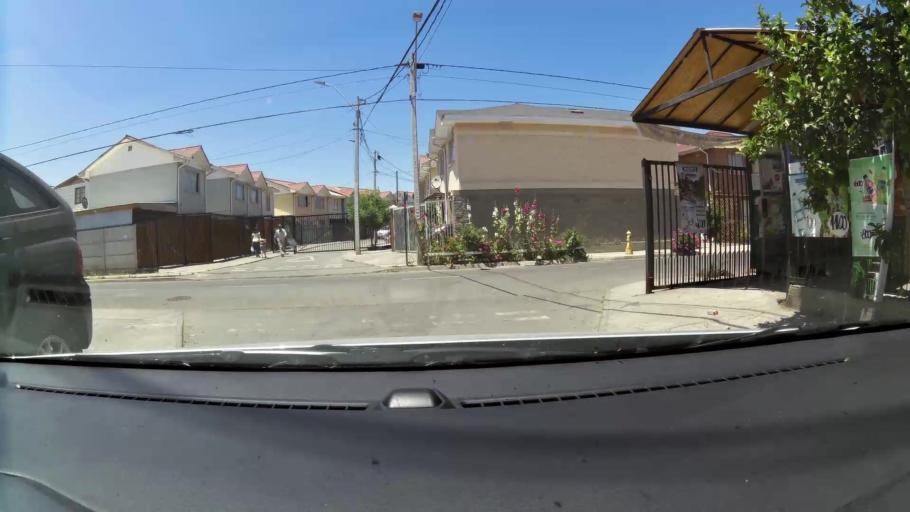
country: CL
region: Santiago Metropolitan
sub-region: Provincia de Maipo
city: San Bernardo
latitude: -33.6040
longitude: -70.6714
